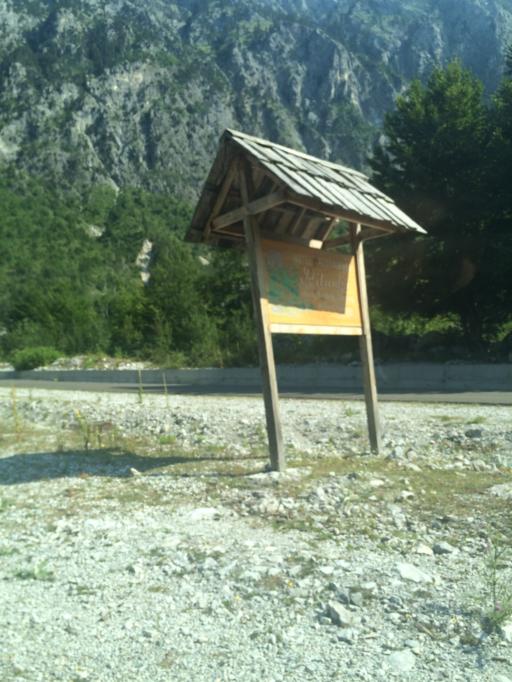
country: AL
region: Kukes
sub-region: Rrethi i Tropojes
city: Valbone
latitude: 42.4601
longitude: 19.9229
